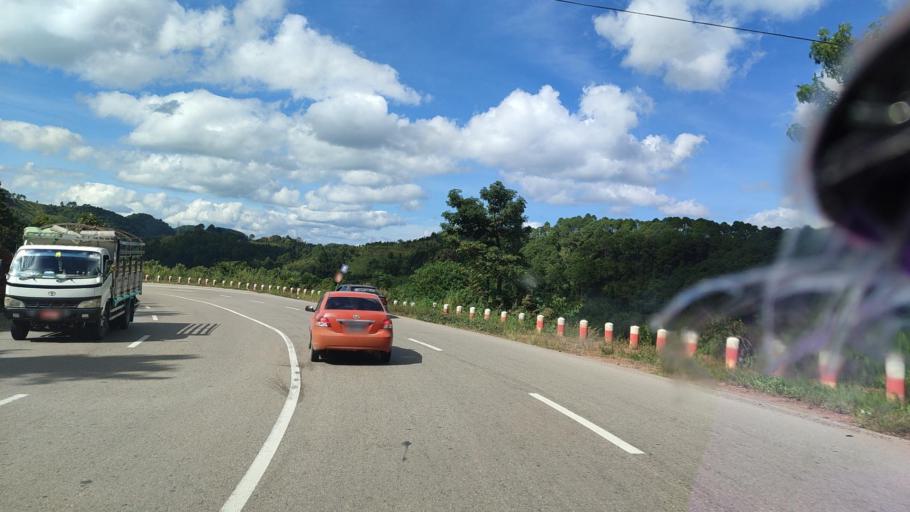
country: MM
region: Mandalay
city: Yamethin
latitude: 20.6561
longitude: 96.5469
